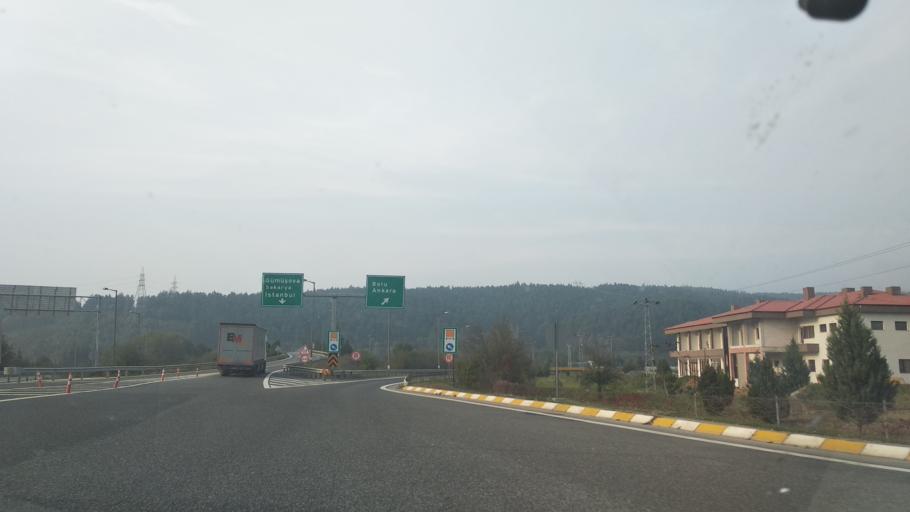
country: TR
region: Duzce
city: Kaynasli
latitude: 40.7846
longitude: 31.2775
